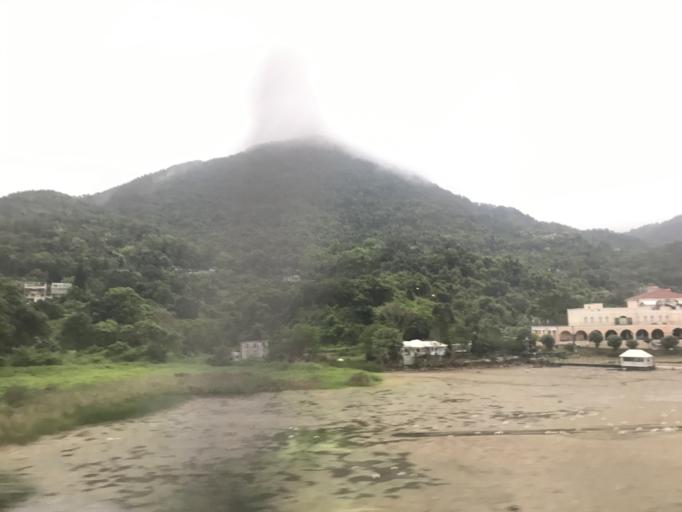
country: HK
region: Tai Po
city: Tai Po
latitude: 22.4374
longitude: 114.1903
